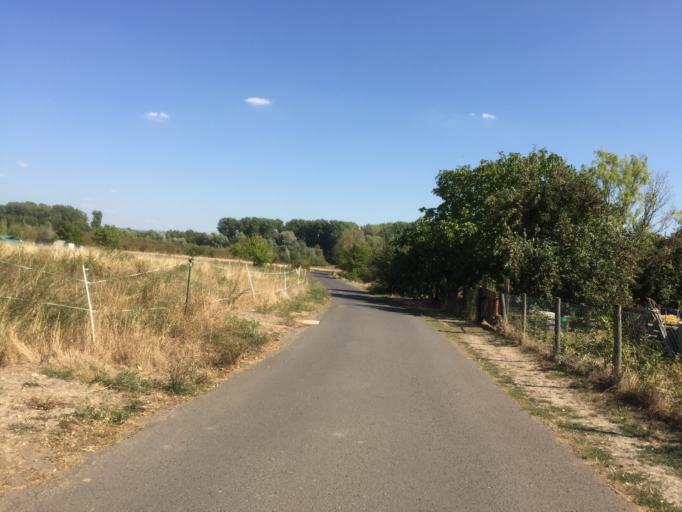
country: DE
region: Hesse
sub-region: Regierungsbezirk Giessen
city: Hungen
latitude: 50.4361
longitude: 8.8910
